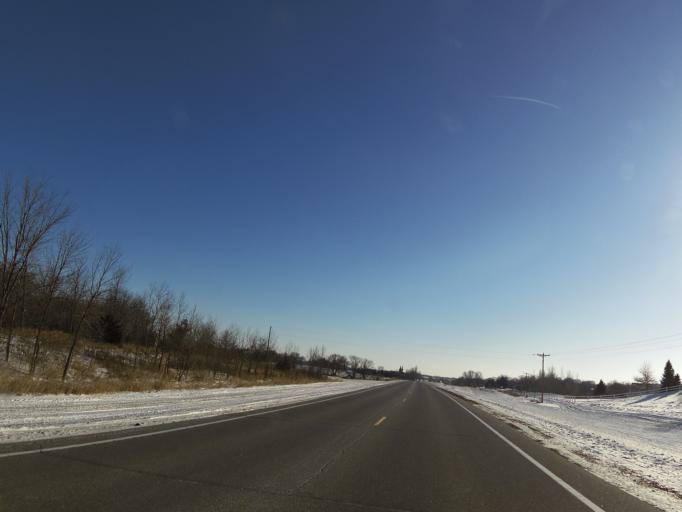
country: US
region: Minnesota
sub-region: Scott County
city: Prior Lake
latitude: 44.6596
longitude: -93.5011
